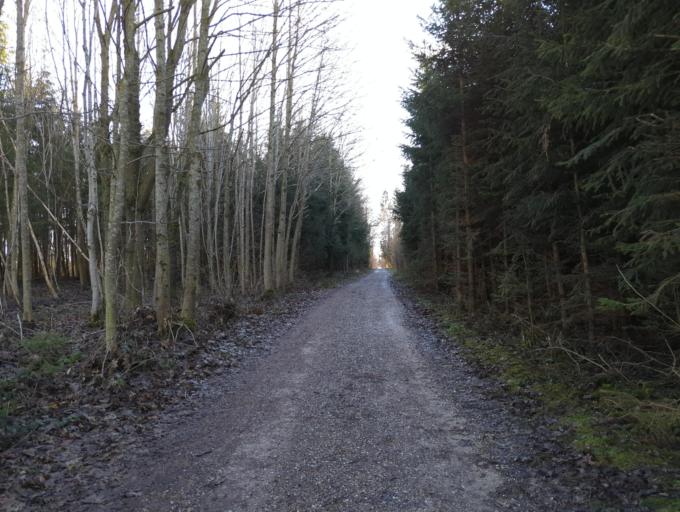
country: DE
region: Bavaria
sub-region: Swabia
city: Roggenburg
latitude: 48.2696
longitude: 10.2159
